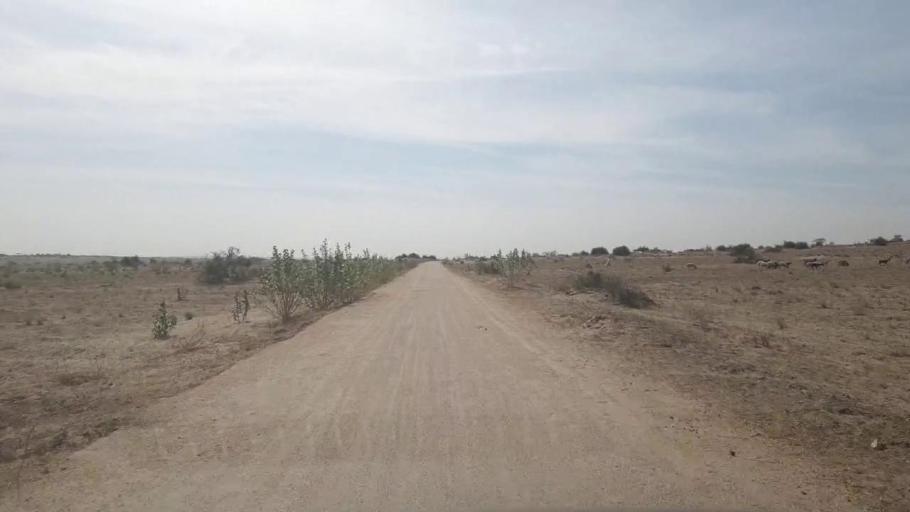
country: PK
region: Sindh
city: Umarkot
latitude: 25.2747
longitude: 69.7311
